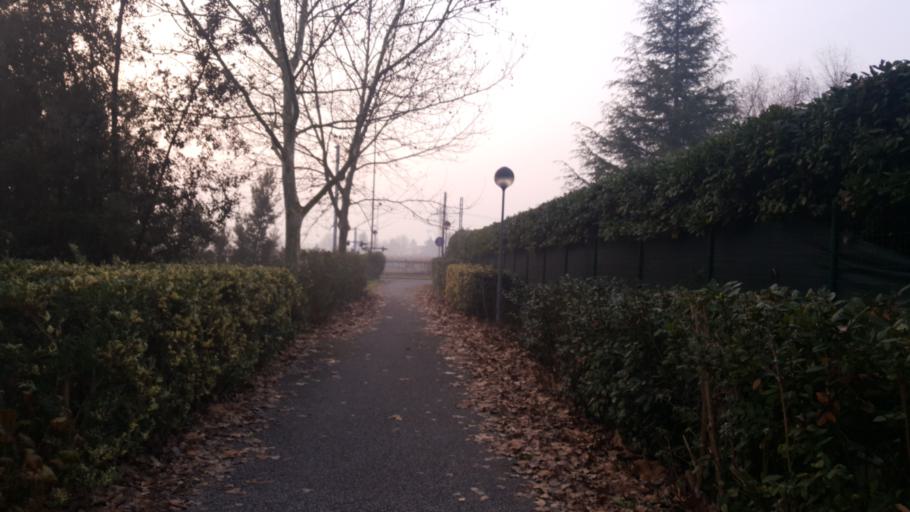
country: IT
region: Emilia-Romagna
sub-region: Provincia di Ravenna
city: Faenza
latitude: 44.3021
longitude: 11.8990
